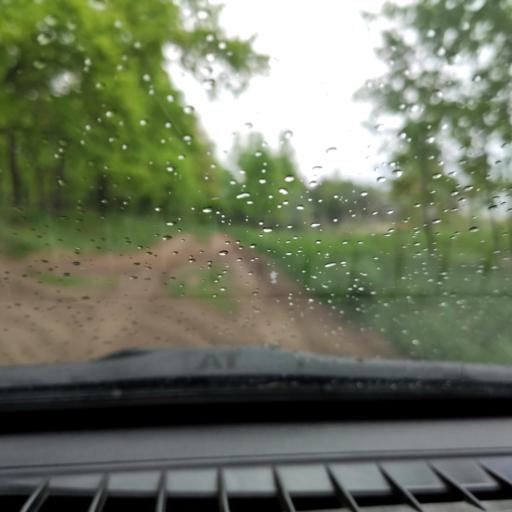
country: RU
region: Samara
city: Zhigulevsk
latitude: 53.5209
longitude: 49.5536
